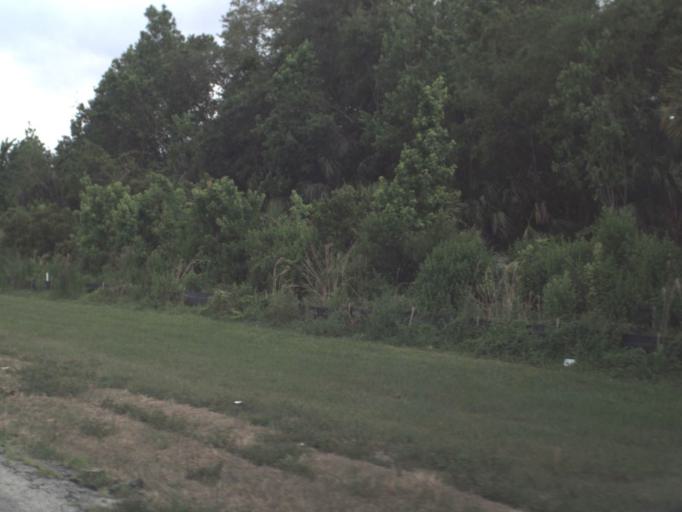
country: US
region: Florida
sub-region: Brevard County
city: Mims
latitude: 28.6393
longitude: -80.8313
